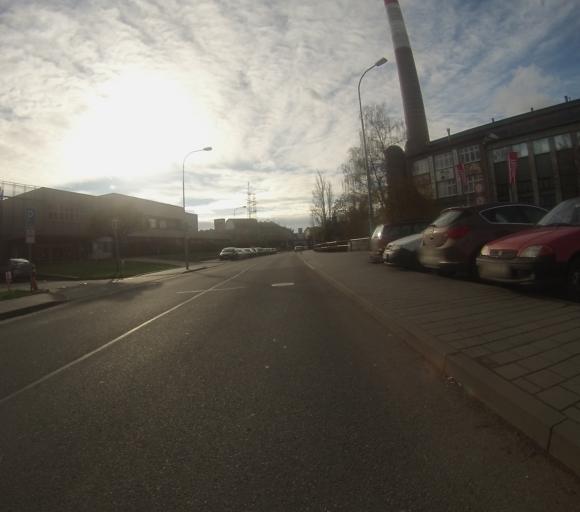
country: CZ
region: South Moravian
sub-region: Mesto Brno
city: Brno
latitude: 49.1961
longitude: 16.6237
